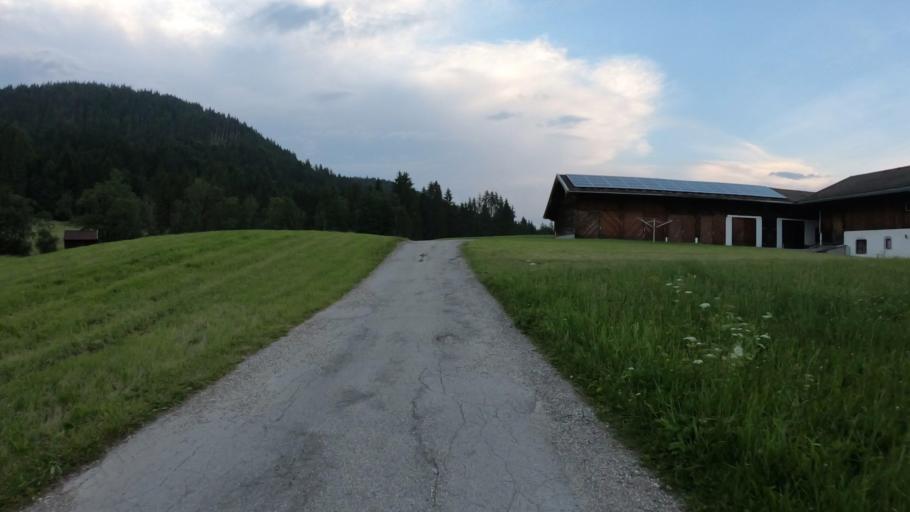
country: DE
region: Bavaria
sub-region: Upper Bavaria
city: Inzell
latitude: 47.7665
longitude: 12.7226
